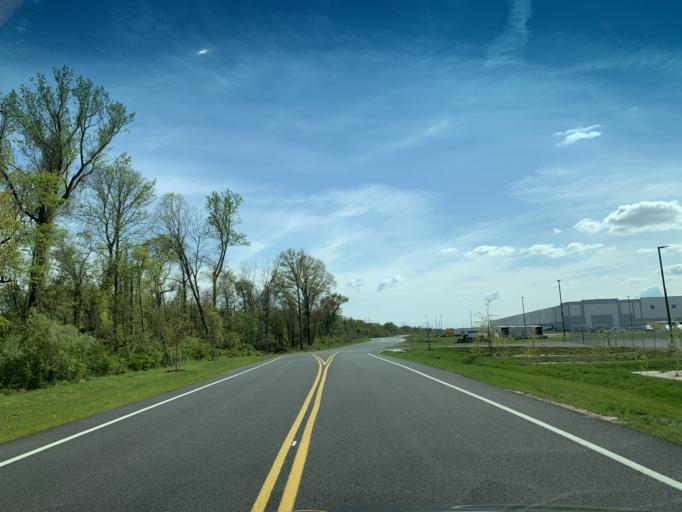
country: US
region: Maryland
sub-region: Harford County
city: Perryman
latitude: 39.4833
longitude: -76.1784
